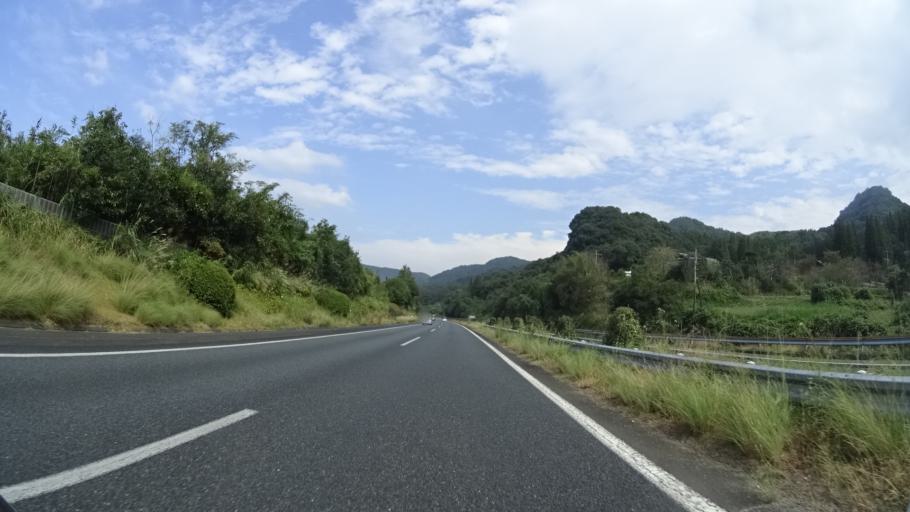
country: JP
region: Kumamoto
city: Matsubase
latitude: 32.5972
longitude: 130.7185
